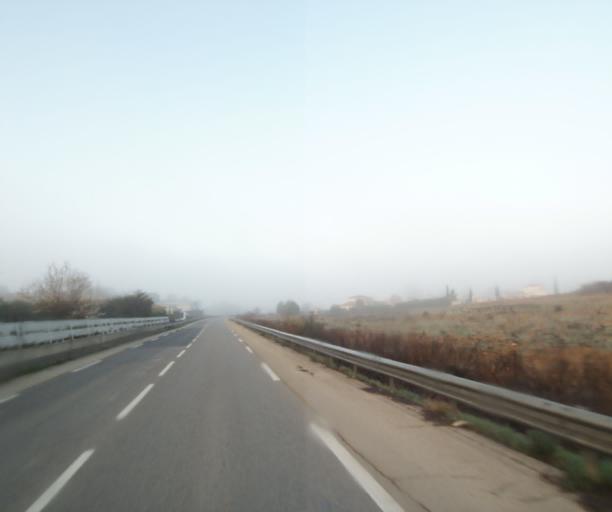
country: FR
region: Provence-Alpes-Cote d'Azur
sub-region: Departement des Bouches-du-Rhone
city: Meyreuil
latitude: 43.4765
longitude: 5.4875
